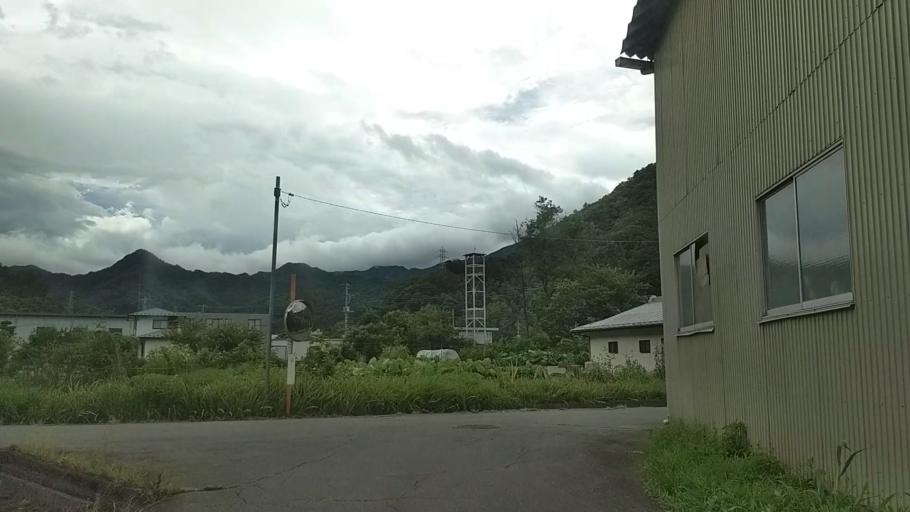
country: JP
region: Yamanashi
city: Otsuki
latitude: 35.5627
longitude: 138.9424
